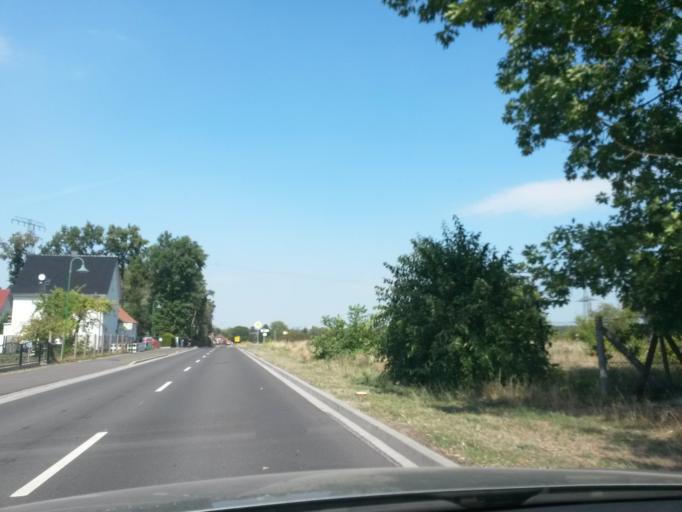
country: DE
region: Saxony-Anhalt
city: Jerichow
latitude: 52.4318
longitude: 11.9972
